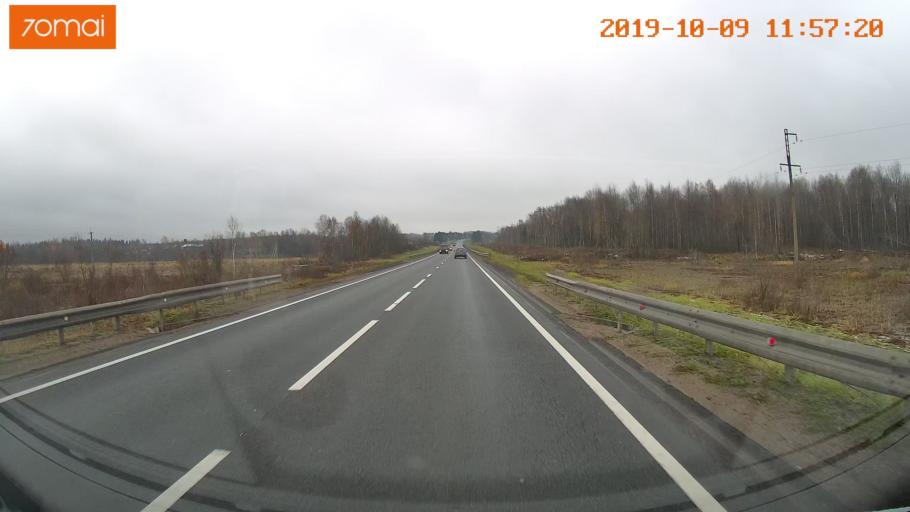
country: RU
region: Vologda
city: Gryazovets
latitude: 58.7336
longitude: 40.2920
